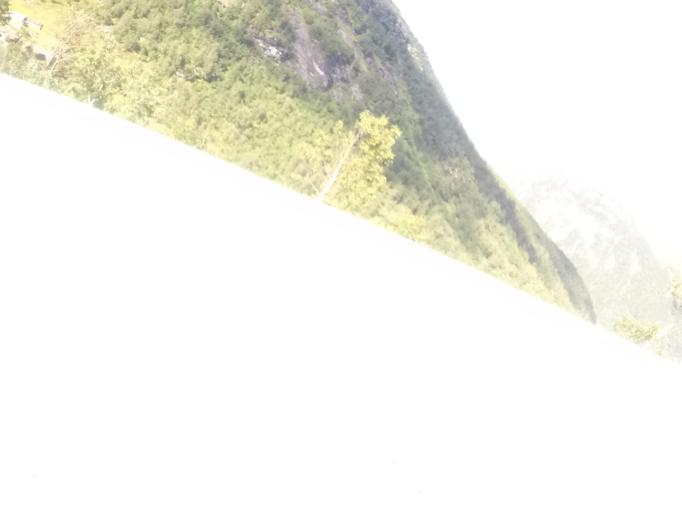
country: NO
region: Sogn og Fjordane
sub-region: Balestrand
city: Balestrand
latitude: 61.3530
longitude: 6.5233
